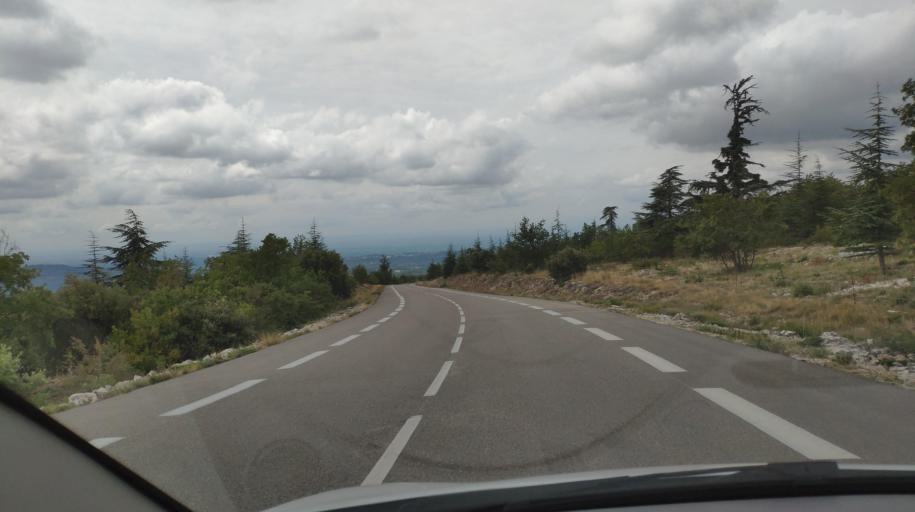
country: FR
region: Provence-Alpes-Cote d'Azur
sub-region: Departement du Vaucluse
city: Villes-sur-Auzon
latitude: 44.0833
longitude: 5.2865
